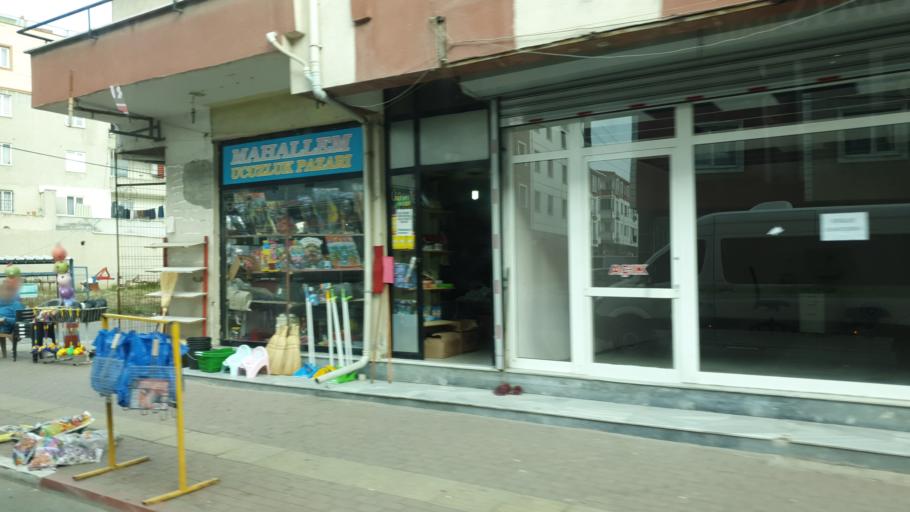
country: TR
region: Tekirdag
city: Muratli
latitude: 41.1763
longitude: 27.5018
